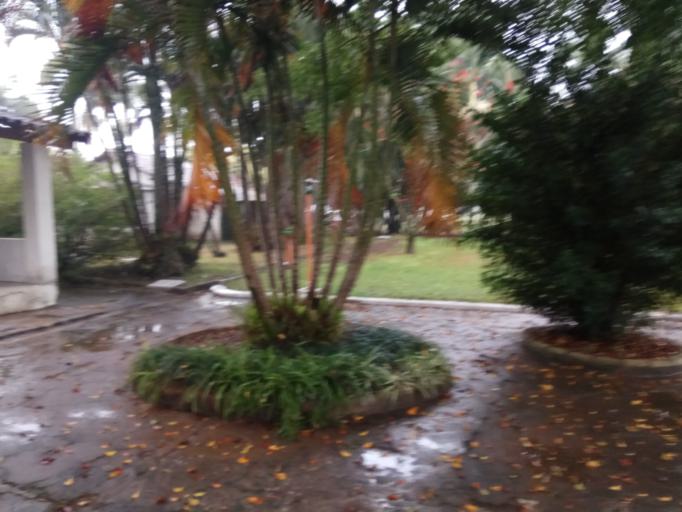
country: BR
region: Sao Paulo
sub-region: Charqueada
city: Charqueada
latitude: -22.4133
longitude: -47.7090
